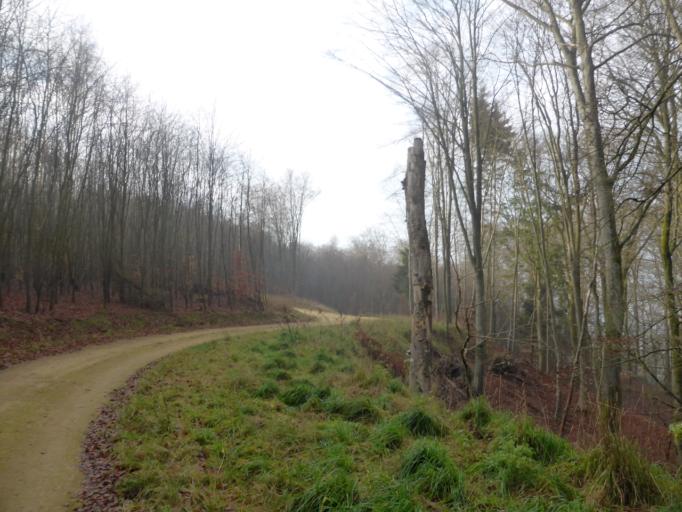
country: LU
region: Luxembourg
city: Rollingen
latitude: 49.7647
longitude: 6.1347
